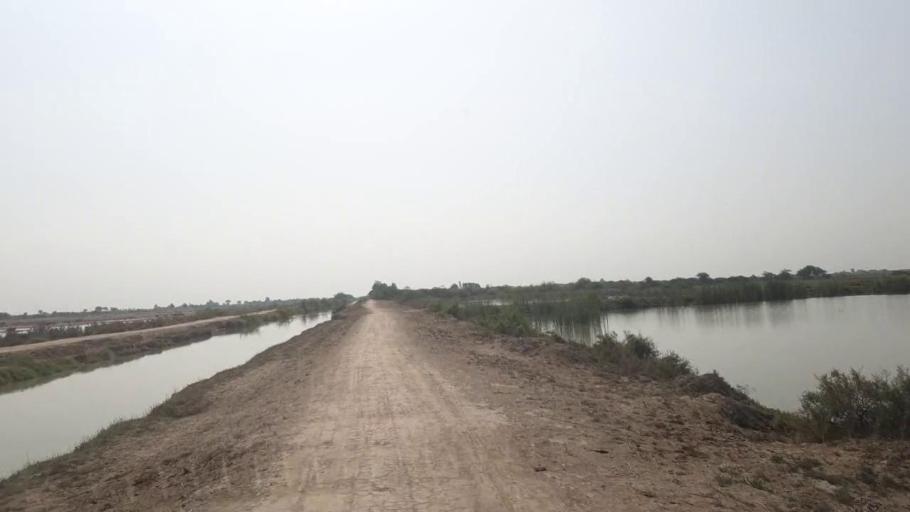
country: PK
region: Sindh
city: Kadhan
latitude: 24.5102
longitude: 68.8504
